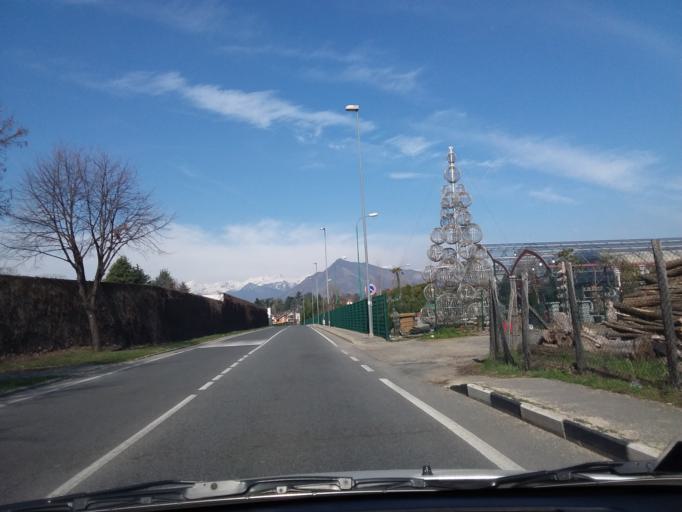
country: IT
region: Piedmont
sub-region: Provincia di Torino
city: Rivoli
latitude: 45.0732
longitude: 7.5300
